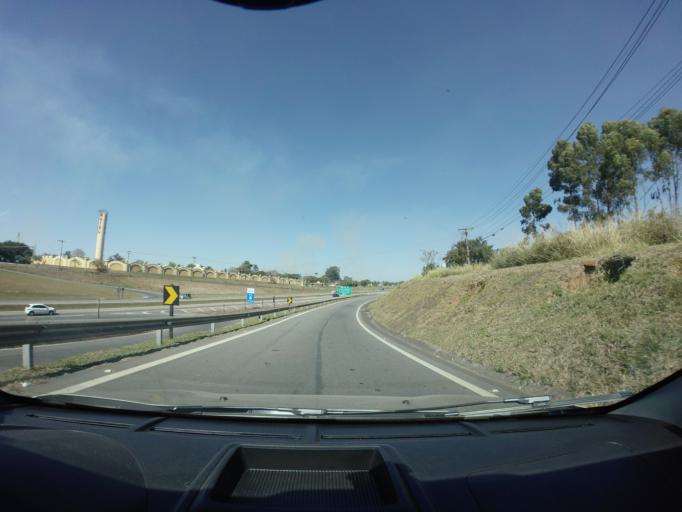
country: BR
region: Sao Paulo
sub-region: Piracicaba
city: Piracicaba
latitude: -22.7367
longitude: -47.6022
